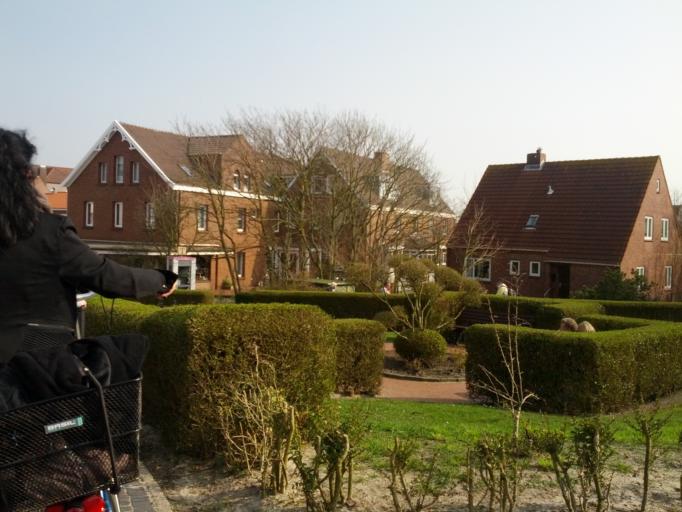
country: DE
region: Lower Saxony
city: Langeoog
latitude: 53.7473
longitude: 7.4773
